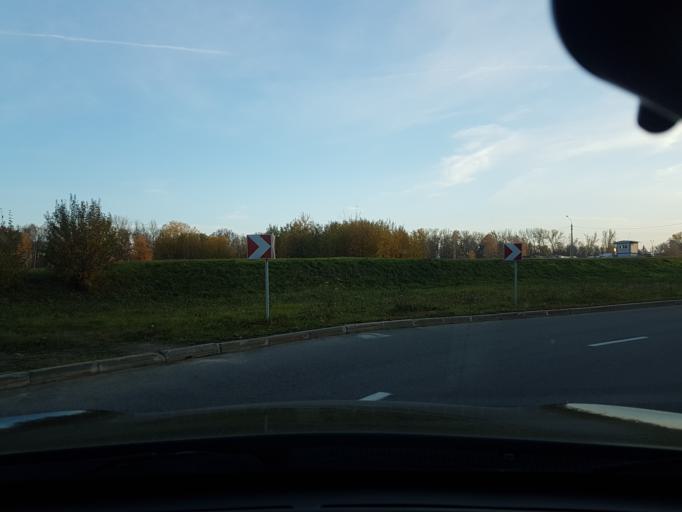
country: BY
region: Minsk
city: Yubilyeyny
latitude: 53.8485
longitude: 27.4907
